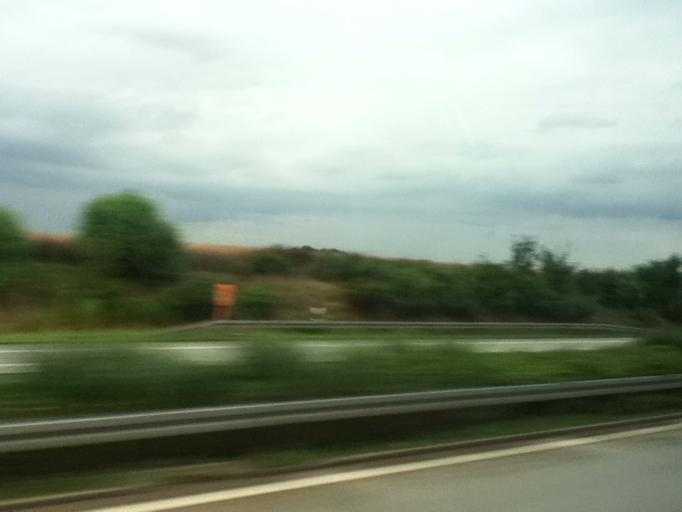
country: DE
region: Thuringia
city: Ponitz
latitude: 50.8271
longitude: 12.4261
